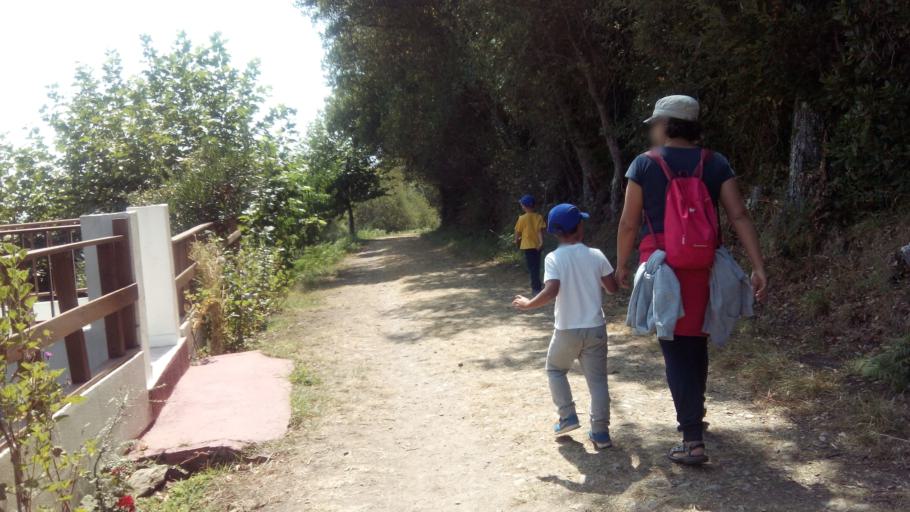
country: ES
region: Galicia
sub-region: Provincia de Pontevedra
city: Sanxenxo
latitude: 42.3792
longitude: -8.9322
